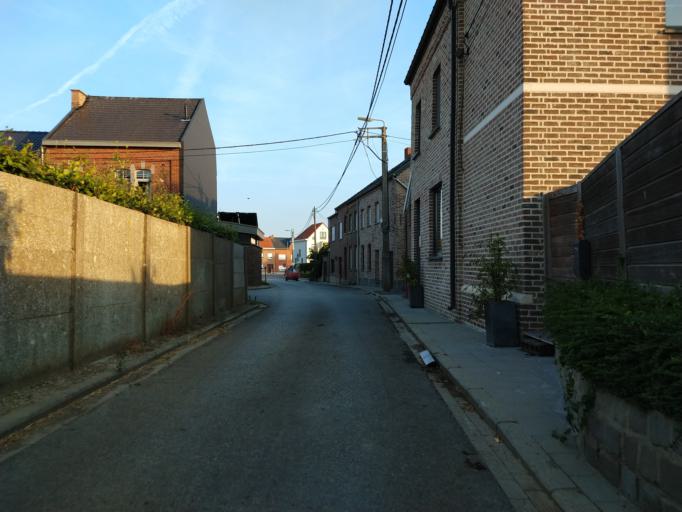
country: BE
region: Flanders
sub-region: Provincie Vlaams-Brabant
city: Hoegaarden
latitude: 50.7824
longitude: 4.8982
